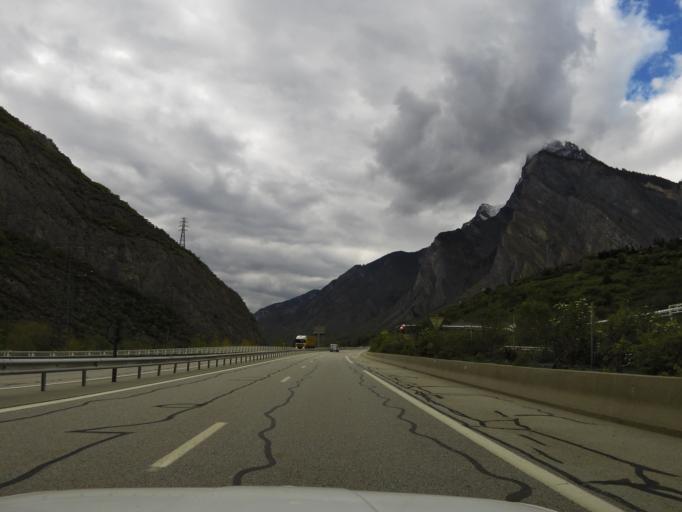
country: FR
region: Rhone-Alpes
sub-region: Departement de la Savoie
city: Saint-Michel-de-Maurienne
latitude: 45.2297
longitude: 6.4486
